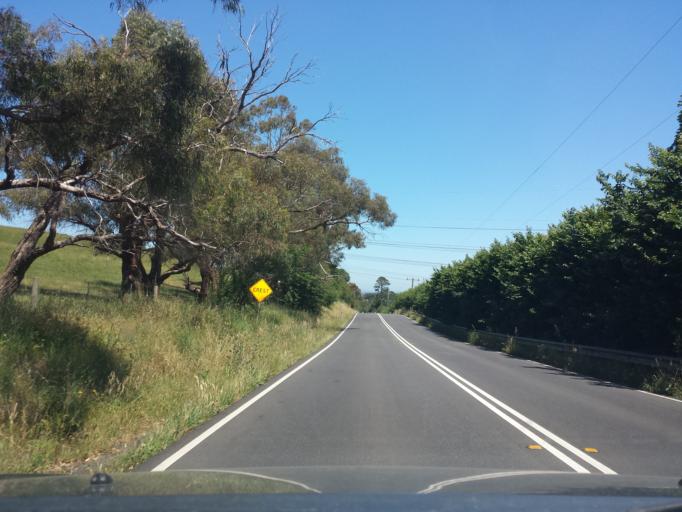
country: AU
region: Victoria
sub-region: Casey
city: Berwick
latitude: -38.0086
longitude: 145.3440
